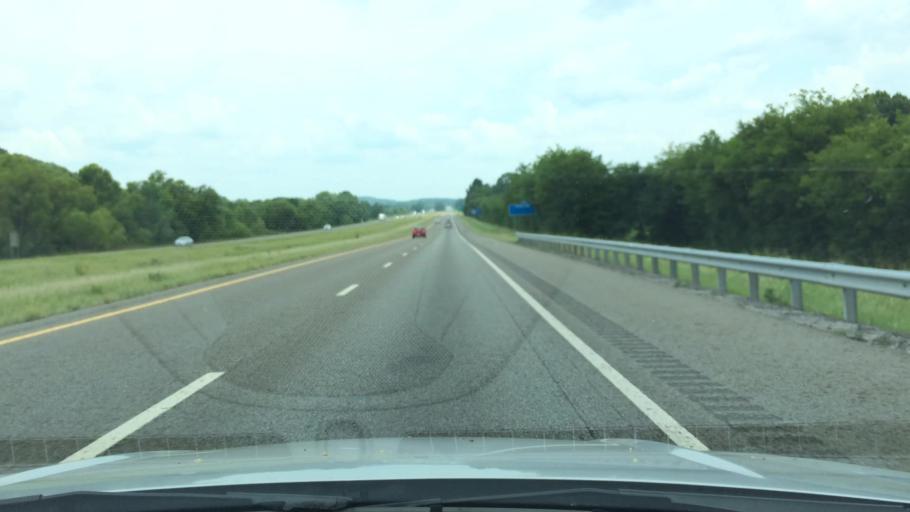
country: US
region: Tennessee
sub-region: Marshall County
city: Cornersville
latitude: 35.4275
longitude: -86.8790
